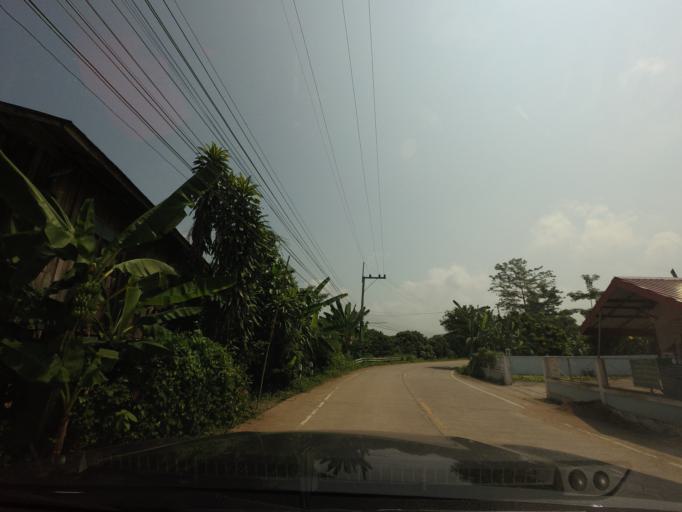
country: TH
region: Nan
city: Nan
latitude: 18.8614
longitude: 100.8142
